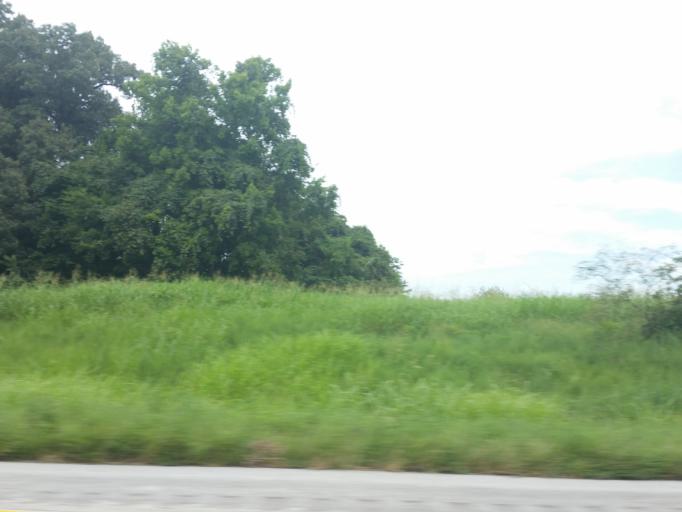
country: US
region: Kentucky
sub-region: Trigg County
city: Cadiz
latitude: 36.9443
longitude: -87.8366
